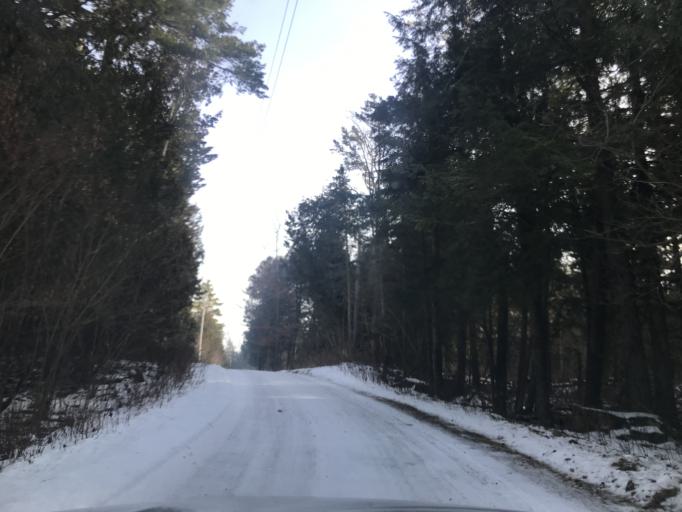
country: US
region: Wisconsin
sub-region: Door County
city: Sturgeon Bay
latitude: 45.1495
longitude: -87.0369
